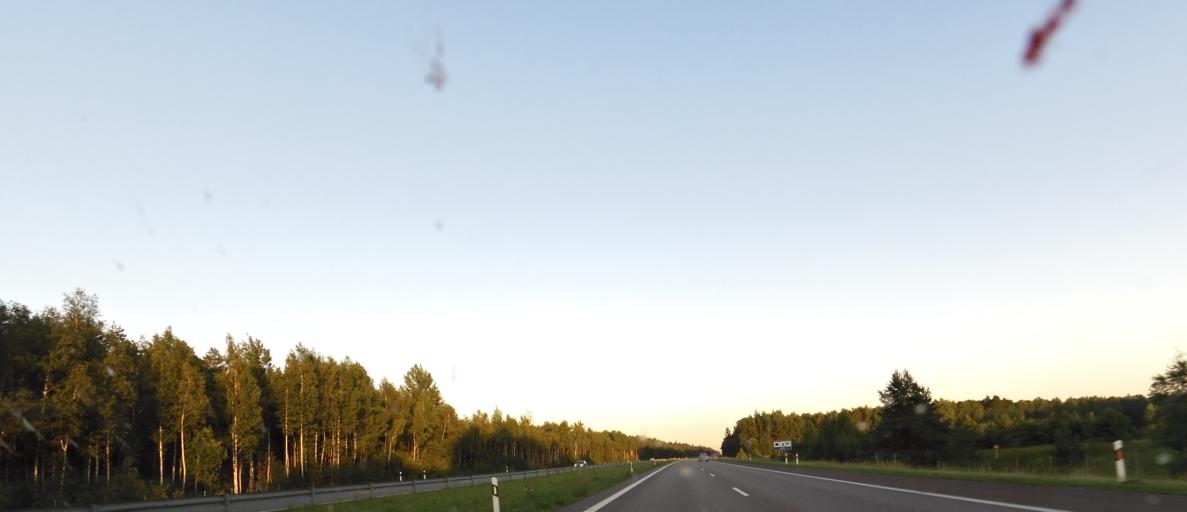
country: LT
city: Sirvintos
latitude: 54.9792
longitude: 24.9404
